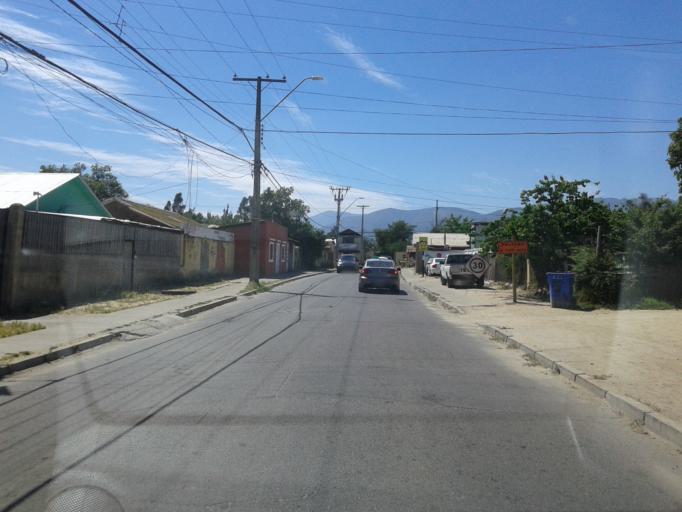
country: CL
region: Valparaiso
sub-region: Provincia de Marga Marga
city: Limache
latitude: -33.0101
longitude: -71.2528
